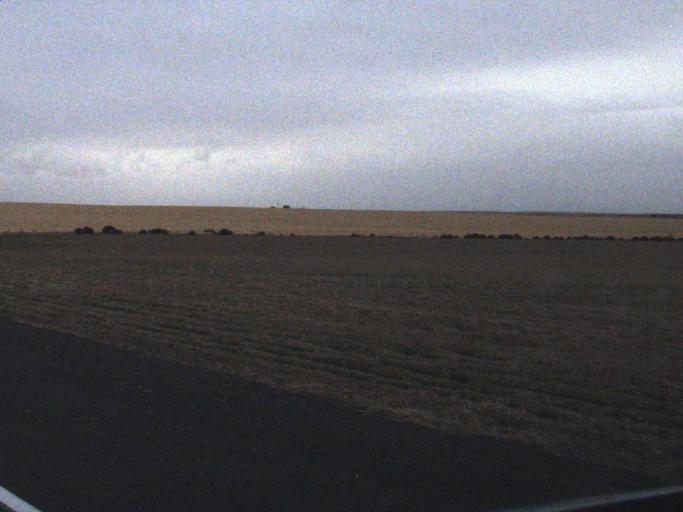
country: US
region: Washington
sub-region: Franklin County
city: Connell
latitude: 46.7945
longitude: -118.6314
